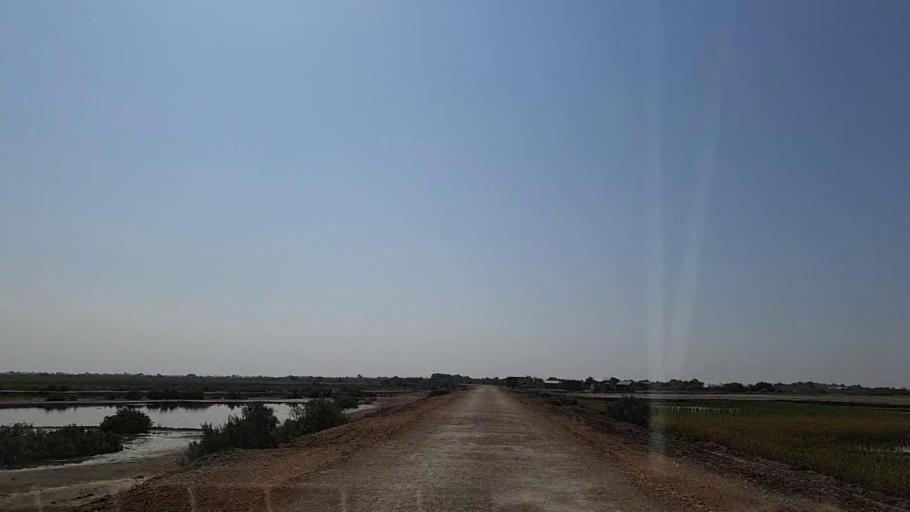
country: PK
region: Sindh
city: Chuhar Jamali
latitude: 24.4760
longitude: 68.0912
